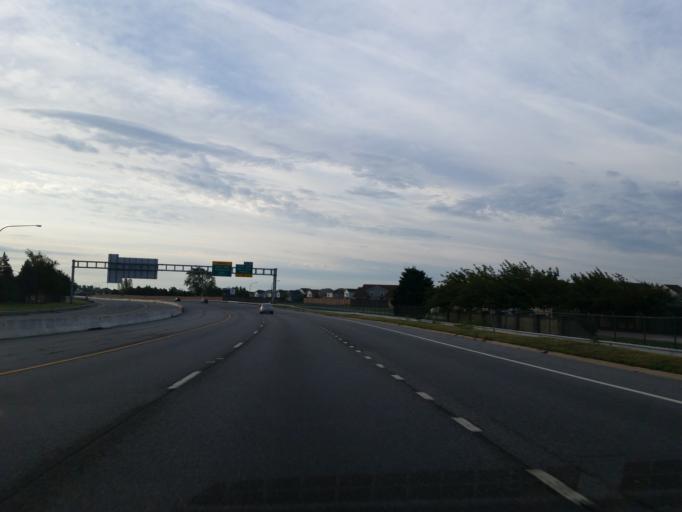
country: US
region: Delaware
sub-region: Kent County
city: Dover Base Housing
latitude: 39.1273
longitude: -75.4894
